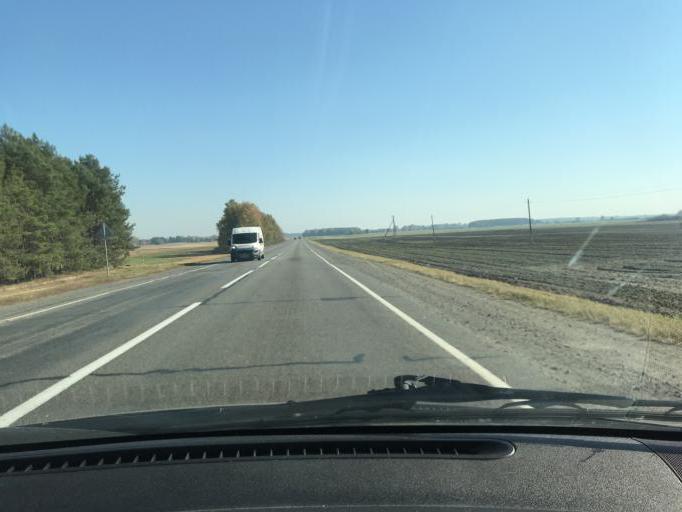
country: BY
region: Brest
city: Davyd-Haradok
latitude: 52.2436
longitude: 27.1615
